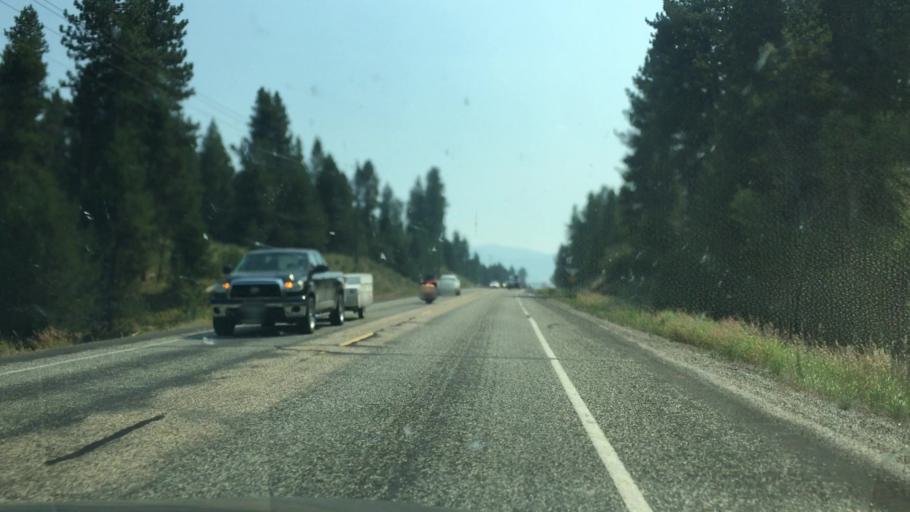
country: US
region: Idaho
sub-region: Valley County
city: Cascade
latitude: 44.3692
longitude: -116.0175
